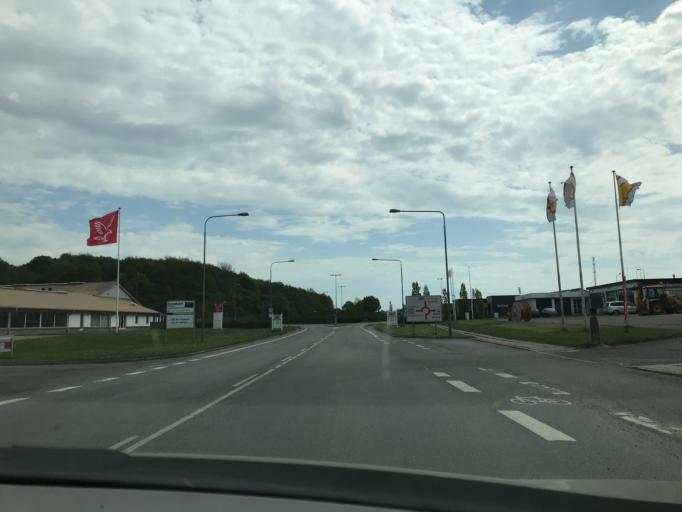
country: DK
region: South Denmark
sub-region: Assens Kommune
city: Assens
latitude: 55.2618
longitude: 9.9102
